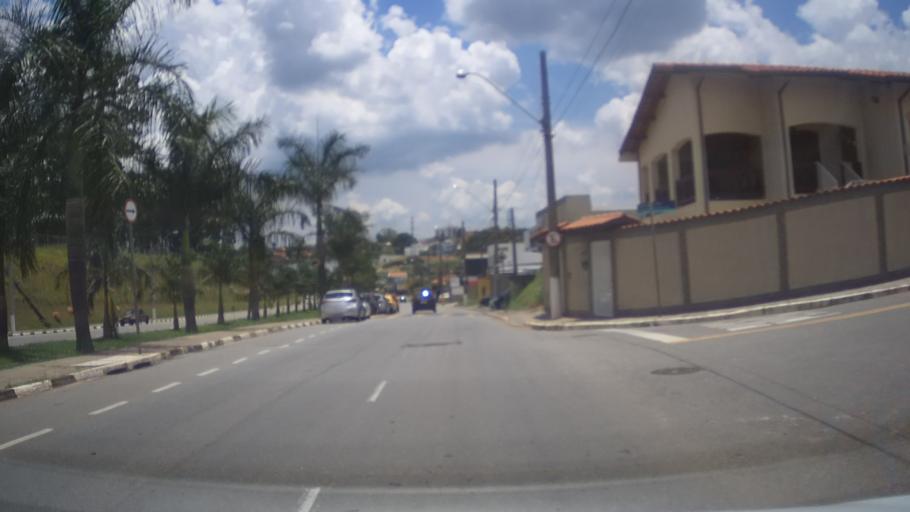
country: BR
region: Sao Paulo
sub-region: Vinhedo
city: Vinhedo
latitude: -23.0389
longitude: -46.9786
